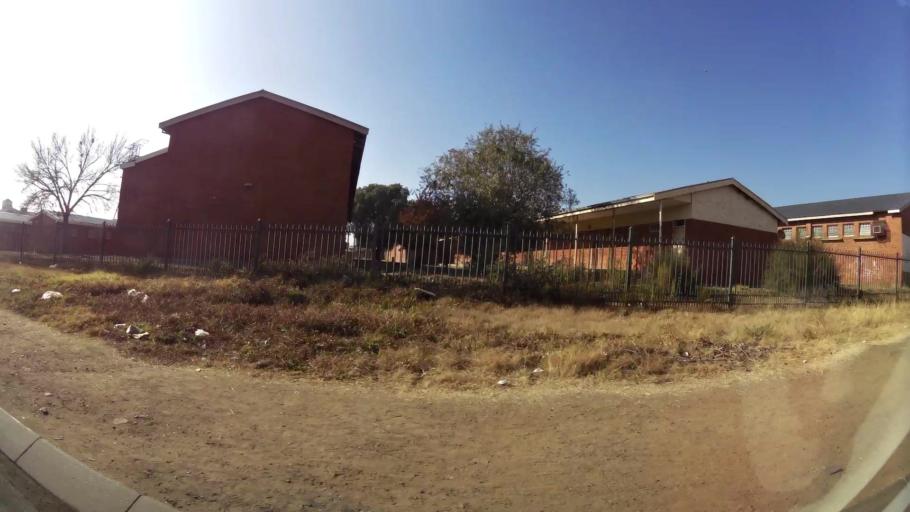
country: ZA
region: Orange Free State
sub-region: Mangaung Metropolitan Municipality
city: Bloemfontein
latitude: -29.1702
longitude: 26.2331
